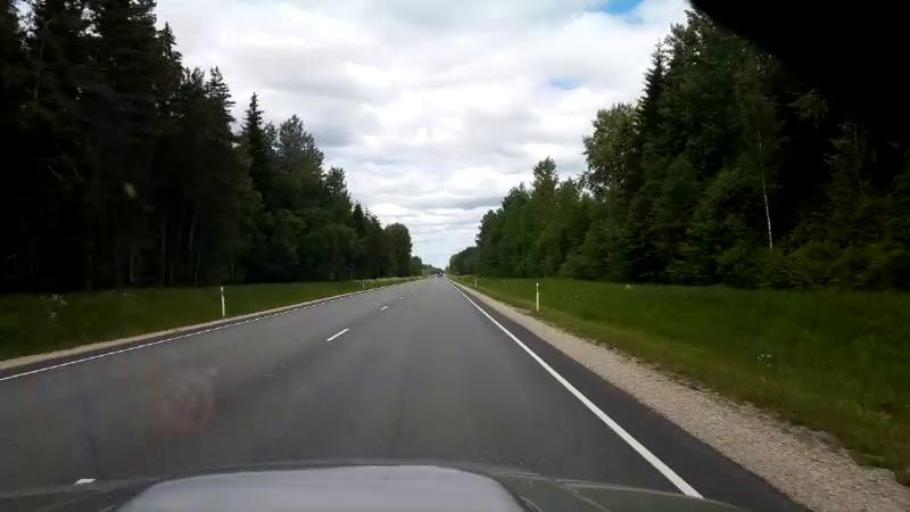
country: EE
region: Raplamaa
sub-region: Maerjamaa vald
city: Marjamaa
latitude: 58.7974
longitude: 24.4128
